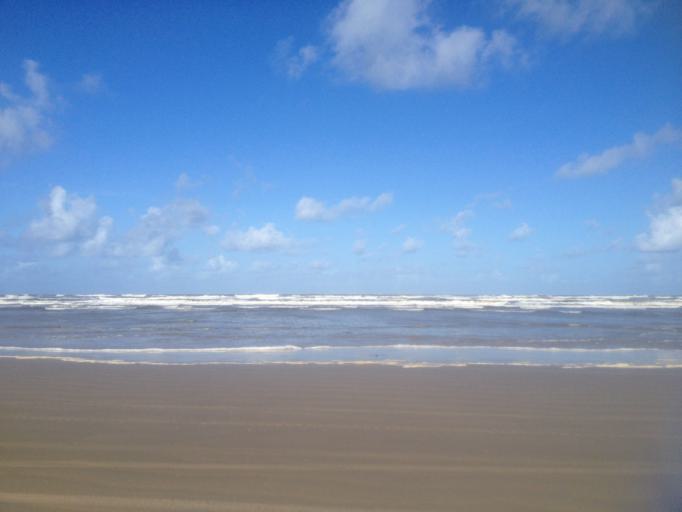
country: BR
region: Sergipe
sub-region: Indiaroba
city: Indiaroba
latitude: -11.4759
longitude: -37.3621
